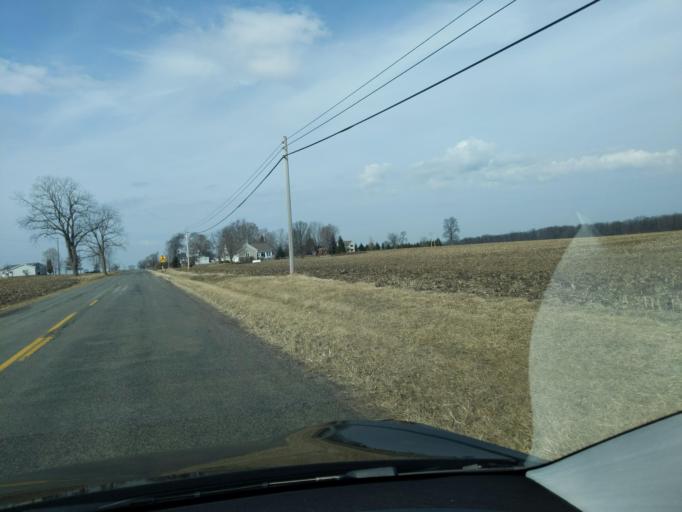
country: US
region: Michigan
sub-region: Ingham County
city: Williamston
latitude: 42.6588
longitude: -84.3079
